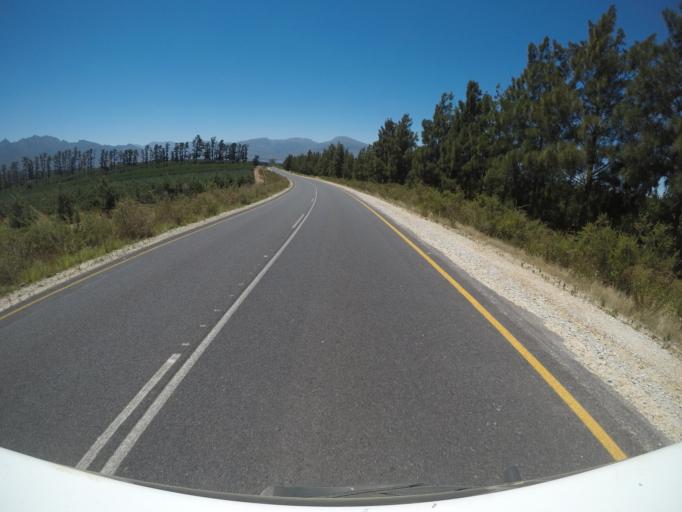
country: ZA
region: Western Cape
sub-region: Overberg District Municipality
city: Grabouw
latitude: -34.0663
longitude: 19.1321
